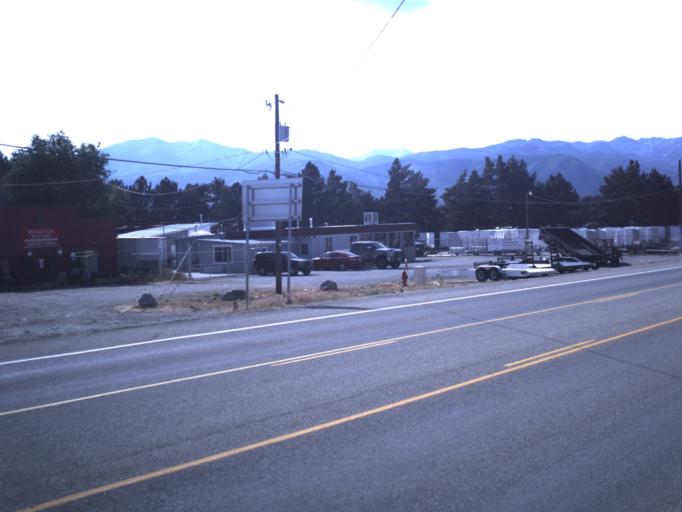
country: US
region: Utah
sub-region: Wasatch County
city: Heber
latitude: 40.4892
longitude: -111.4094
